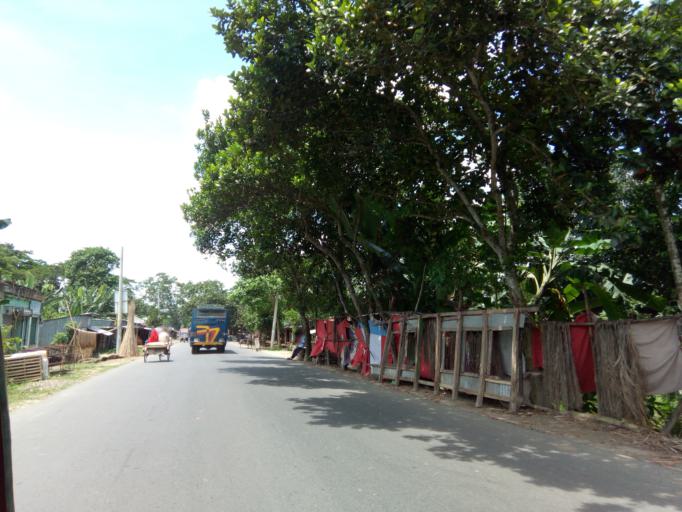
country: BD
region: Dhaka
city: Tungipara
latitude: 22.9067
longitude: 89.8790
